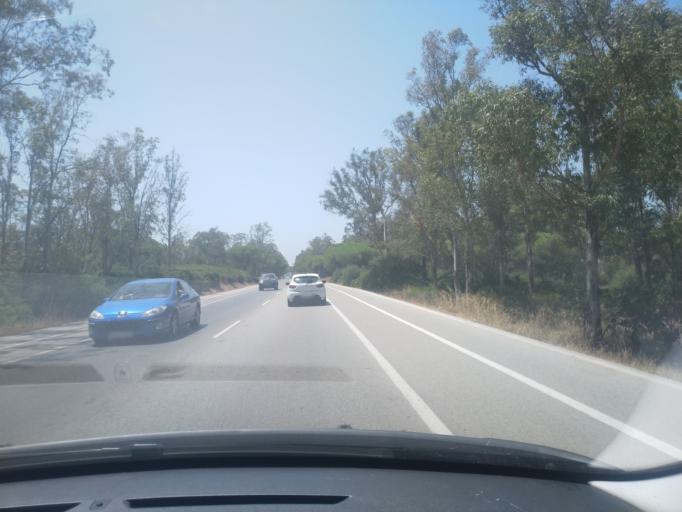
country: ES
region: Andalusia
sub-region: Provincia de Cadiz
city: Chiclana de la Frontera
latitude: 36.3908
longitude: -6.1260
